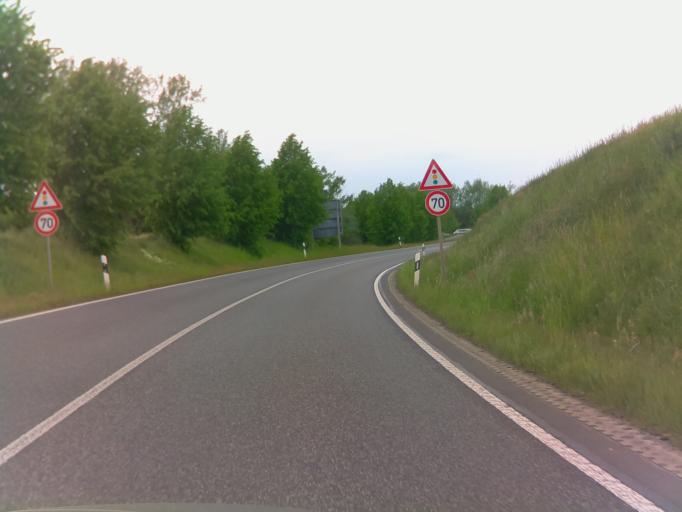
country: DE
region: Hesse
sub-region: Regierungsbezirk Kassel
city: Schrecksbach
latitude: 50.8813
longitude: 9.2662
